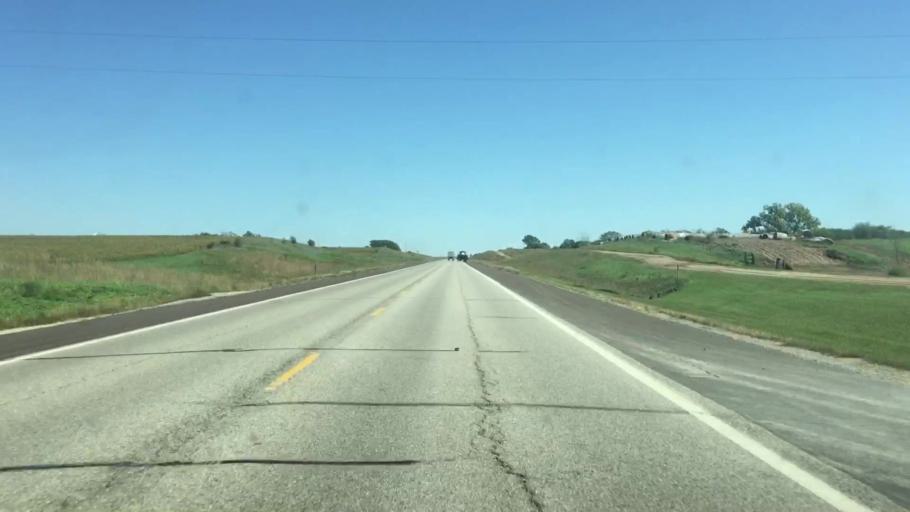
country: US
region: Kansas
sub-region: Nemaha County
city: Seneca
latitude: 39.8421
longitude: -96.2868
